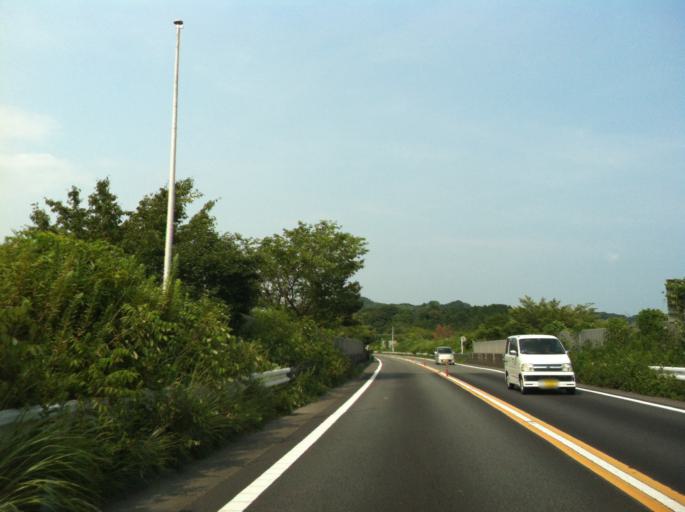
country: JP
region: Shizuoka
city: Fujieda
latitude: 34.8723
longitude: 138.2292
